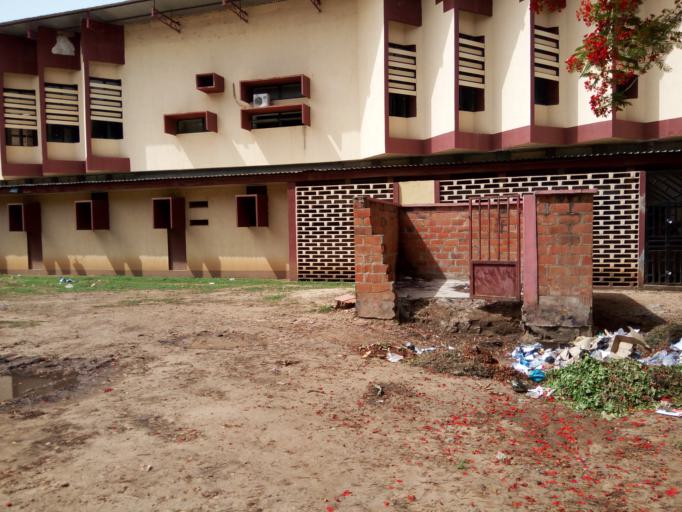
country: NG
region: Kaduna
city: Zaria
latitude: 11.1500
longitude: 7.6525
